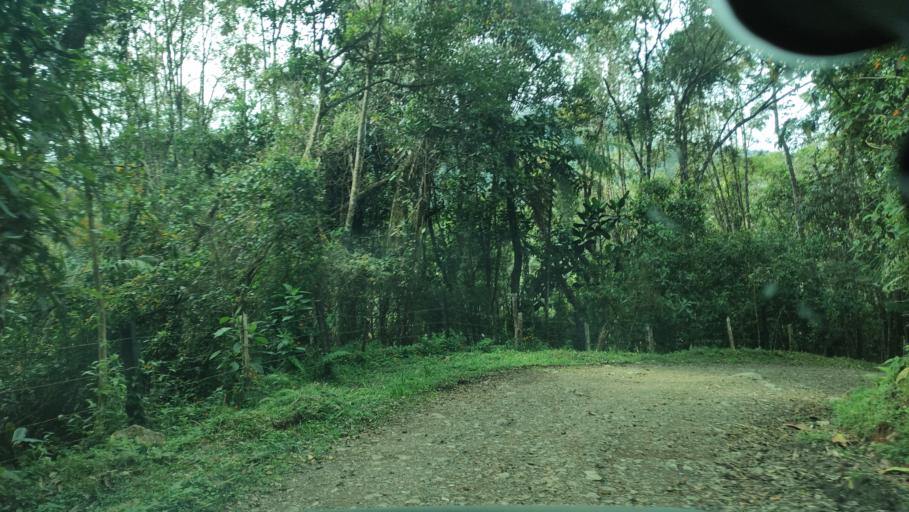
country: CO
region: Valle del Cauca
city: Cali
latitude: 3.4495
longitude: -76.6631
